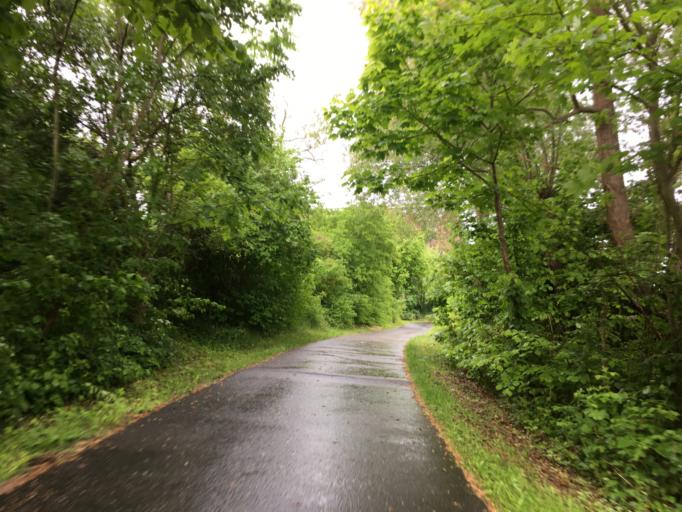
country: DE
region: Brandenburg
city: Eberswalde
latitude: 52.8404
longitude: 13.7452
